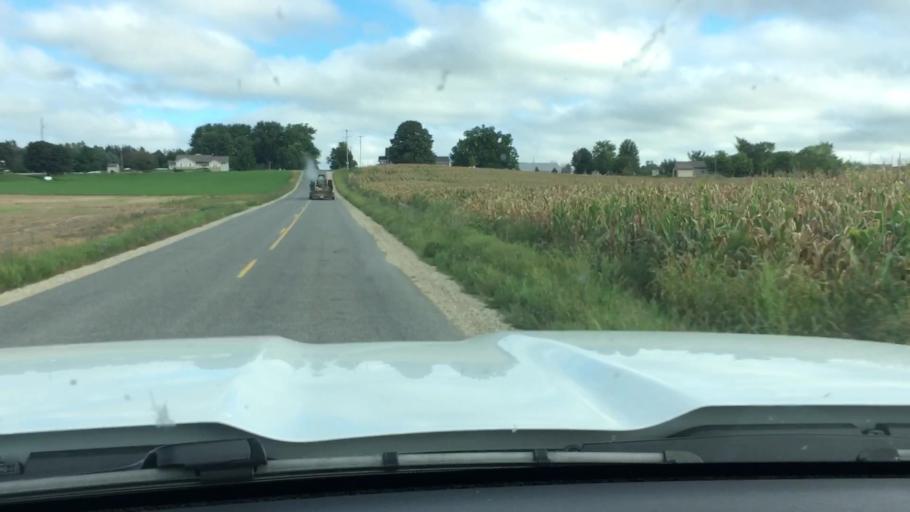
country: US
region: Michigan
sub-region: Kent County
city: Byron Center
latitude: 42.7945
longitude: -85.8027
